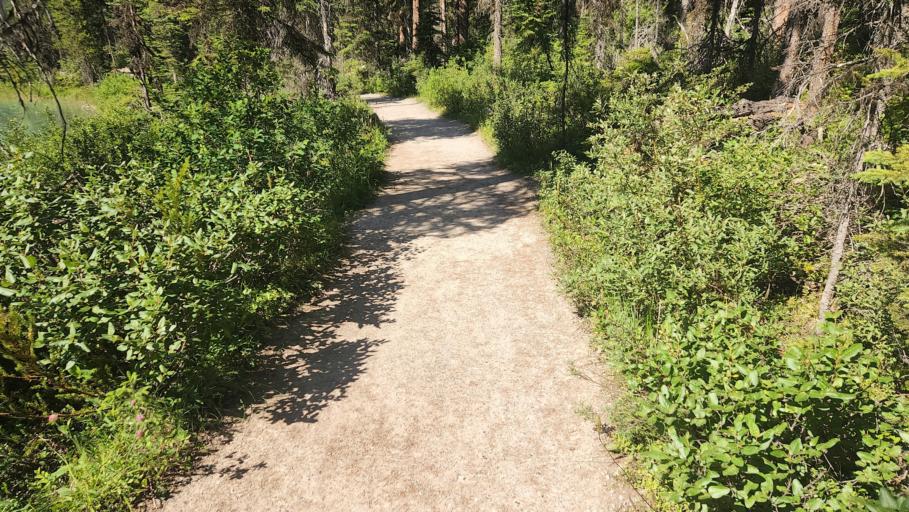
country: CA
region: Alberta
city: Lake Louise
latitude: 51.4451
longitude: -116.5364
